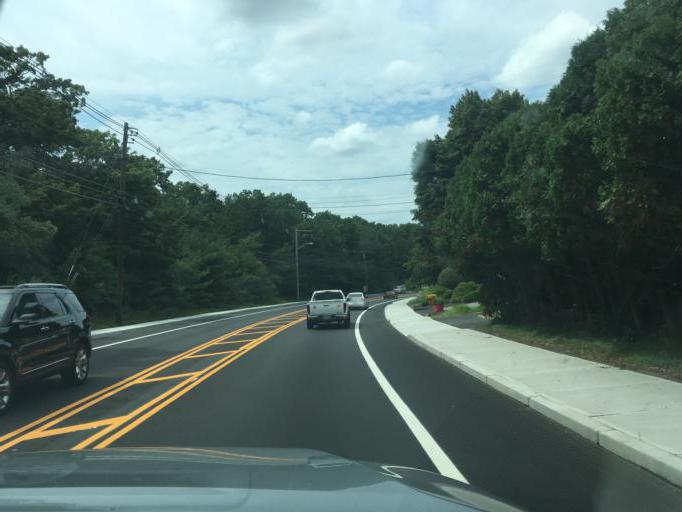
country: US
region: Rhode Island
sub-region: Kent County
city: West Warwick
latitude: 41.6670
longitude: -71.5491
